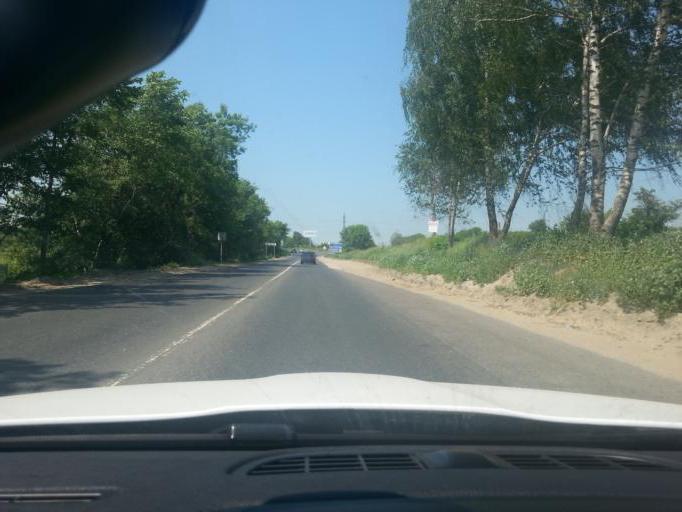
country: RU
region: Moscow
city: Nekrasovka
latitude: 55.7105
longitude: 37.9562
